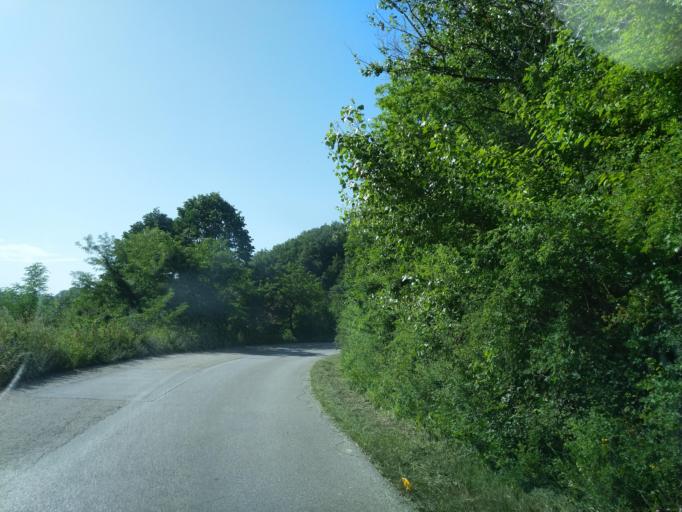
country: RS
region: Central Serbia
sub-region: Zlatiborski Okrug
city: Cajetina
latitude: 43.8689
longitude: 19.6988
